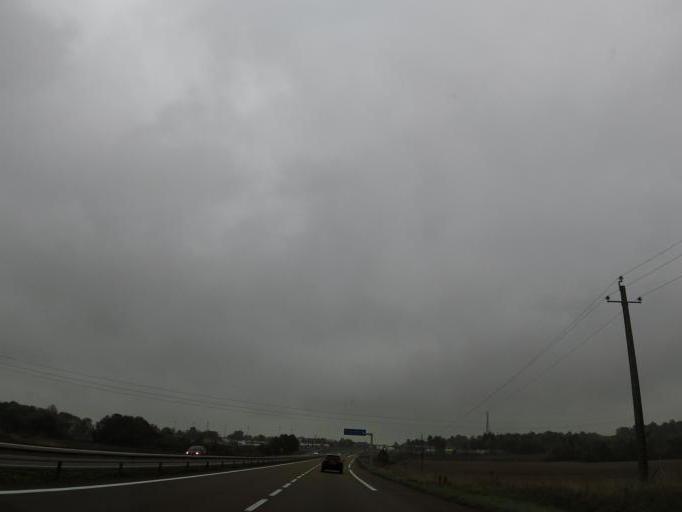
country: FR
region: Champagne-Ardenne
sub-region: Departement de la Marne
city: Verzy
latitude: 49.1240
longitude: 4.2378
